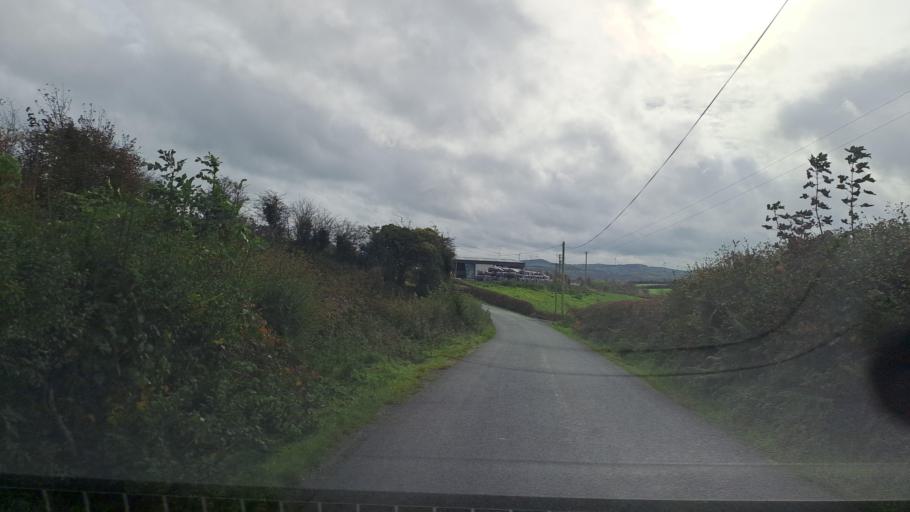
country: IE
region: Ulster
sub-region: An Cabhan
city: Bailieborough
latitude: 54.0153
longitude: -6.8989
